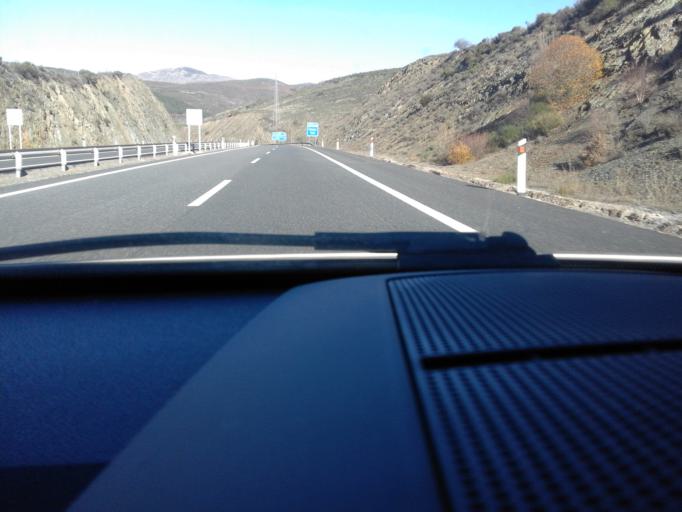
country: ES
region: Castille and Leon
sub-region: Provincia de Leon
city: Carrocera
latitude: 42.7727
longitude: -5.7818
